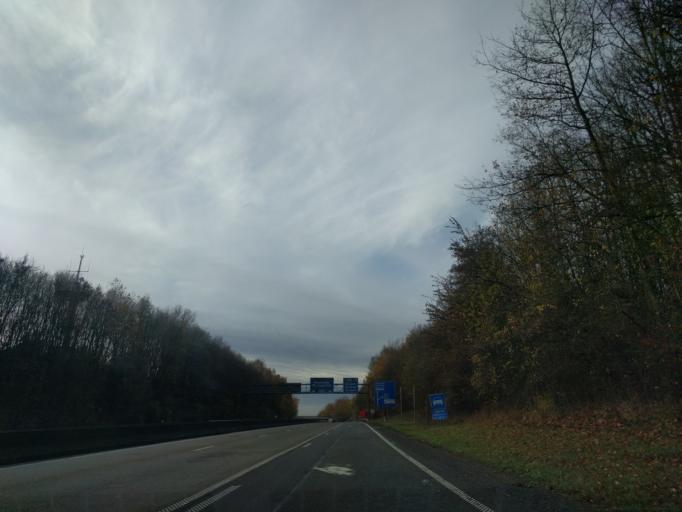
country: BE
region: Wallonia
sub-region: Province de Namur
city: Ciney
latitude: 50.2660
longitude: 5.0326
